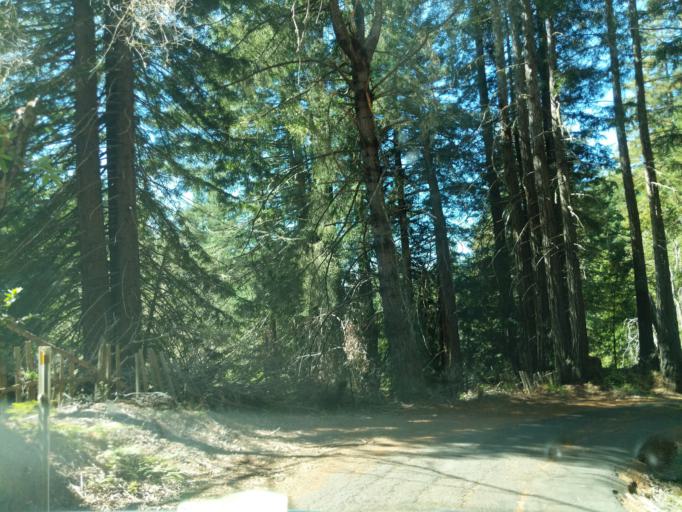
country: US
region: California
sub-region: Sonoma County
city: Monte Rio
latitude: 38.5236
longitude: -123.2319
